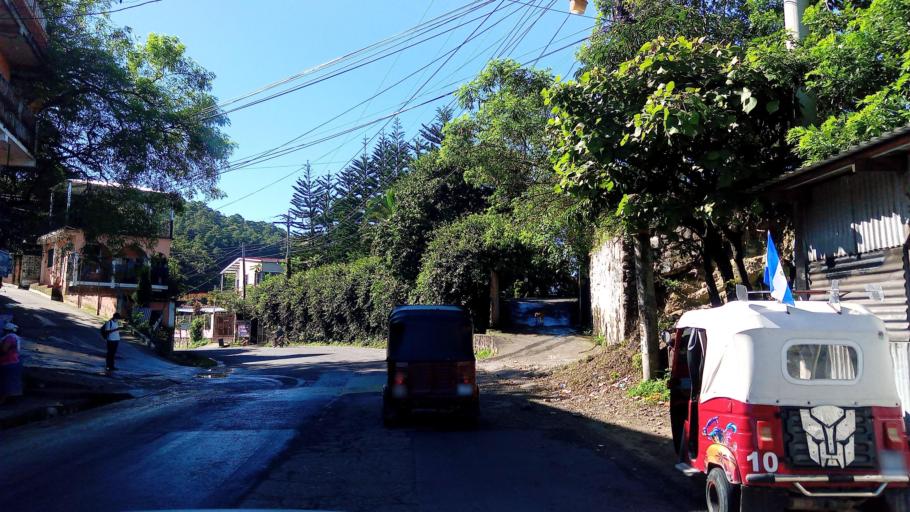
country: HN
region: Ocotepeque
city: Antigua Ocotepeque
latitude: 14.3132
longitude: -89.1631
